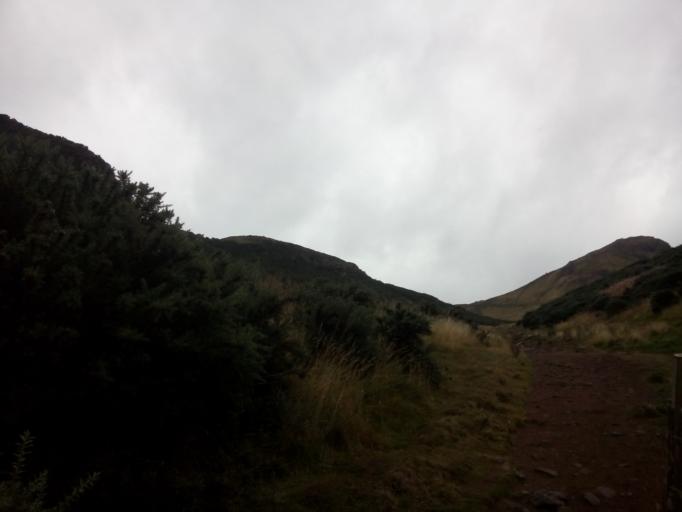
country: GB
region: Scotland
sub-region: West Lothian
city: Seafield
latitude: 55.9500
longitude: -3.1618
